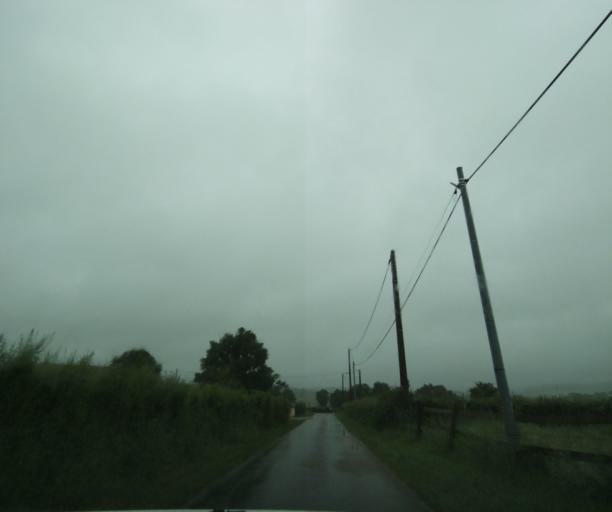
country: FR
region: Bourgogne
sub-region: Departement de Saone-et-Loire
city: Charolles
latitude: 46.4038
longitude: 4.2614
